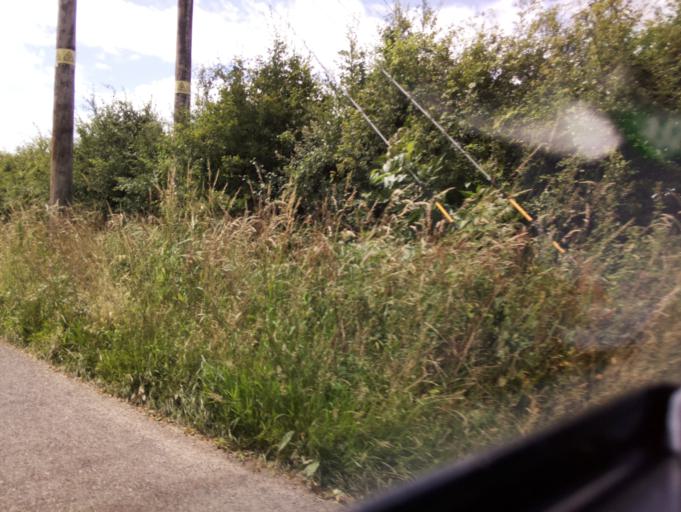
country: GB
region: England
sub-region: Nottinghamshire
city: Ruddington
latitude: 52.8664
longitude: -1.0933
